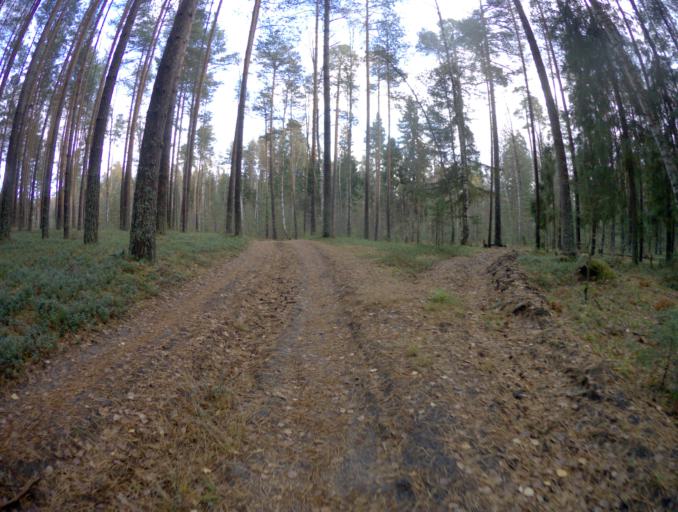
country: RU
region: Vladimir
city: Raduzhnyy
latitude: 56.0568
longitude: 40.3246
